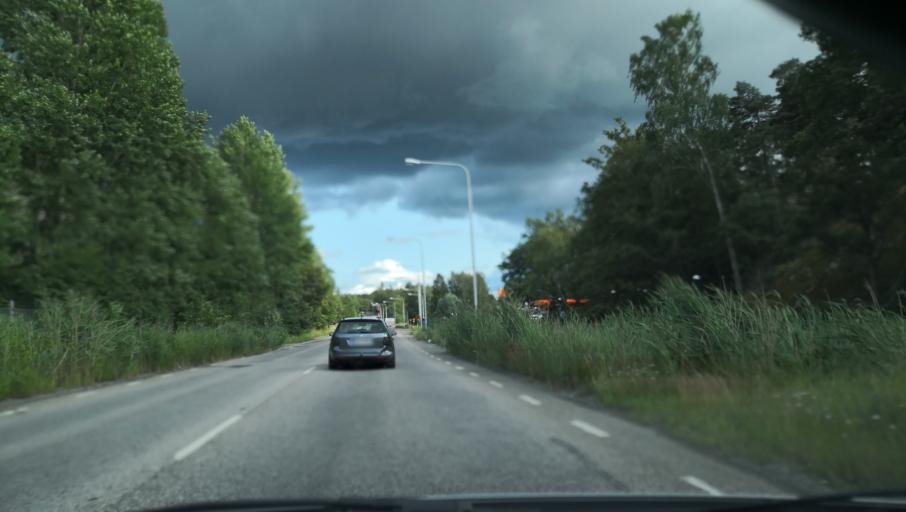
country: SE
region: Stockholm
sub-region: Stockholms Kommun
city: Arsta
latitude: 59.2494
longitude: 18.0631
